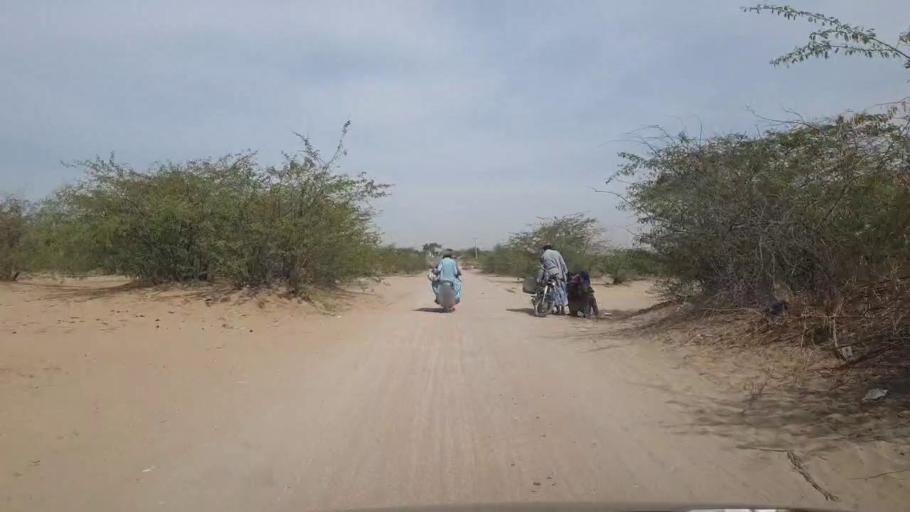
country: PK
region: Sindh
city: Umarkot
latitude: 25.2950
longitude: 69.7278
